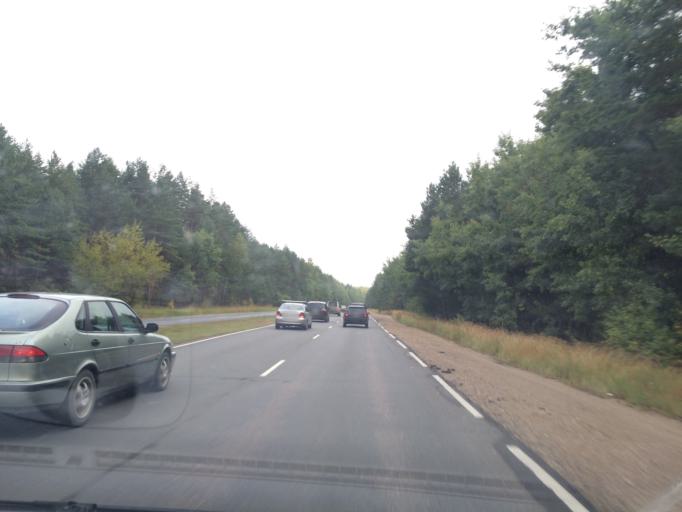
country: LV
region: Salaspils
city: Salaspils
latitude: 56.8632
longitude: 24.2946
